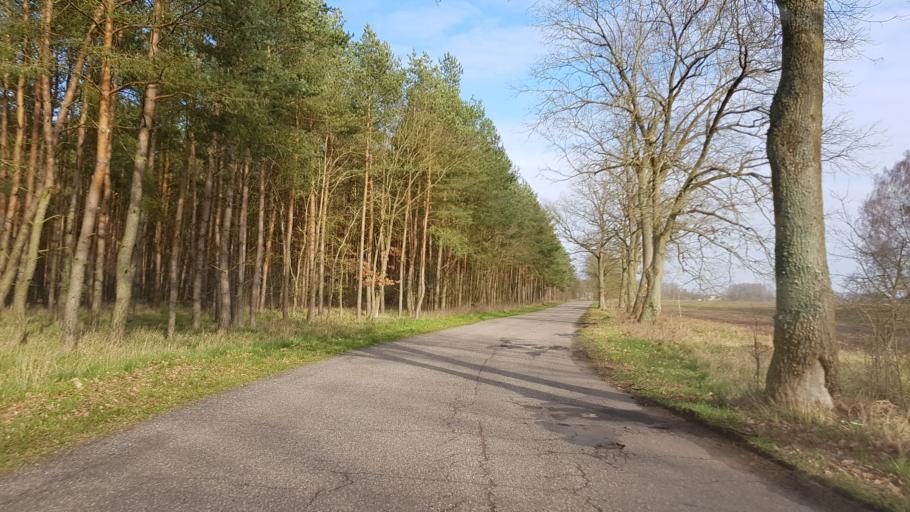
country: PL
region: West Pomeranian Voivodeship
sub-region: Powiat policki
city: Dobra
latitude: 53.5280
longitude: 14.3246
